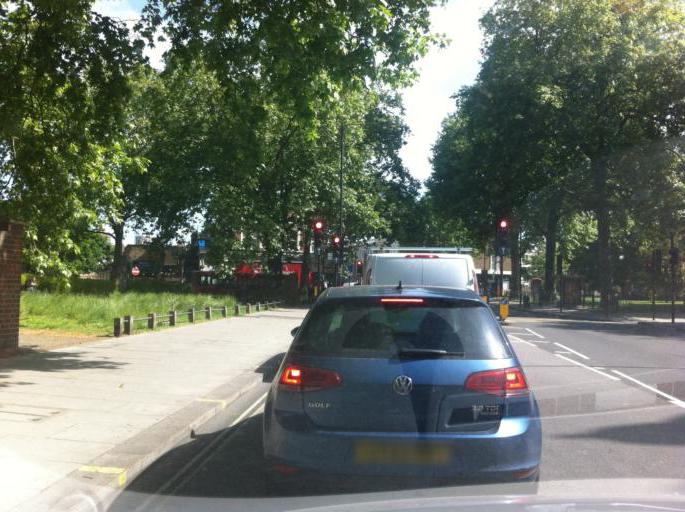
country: GB
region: England
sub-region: Greater London
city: Hammersmith
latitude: 51.4965
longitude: -0.2236
